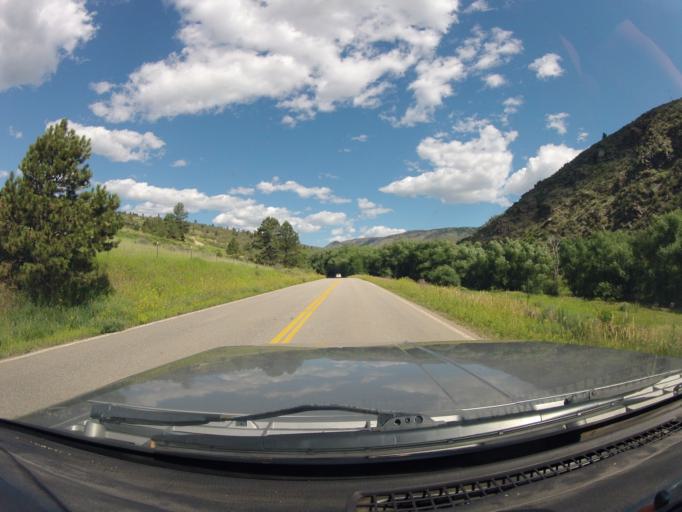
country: US
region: Colorado
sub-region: Larimer County
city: Laporte
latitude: 40.5405
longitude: -105.2796
